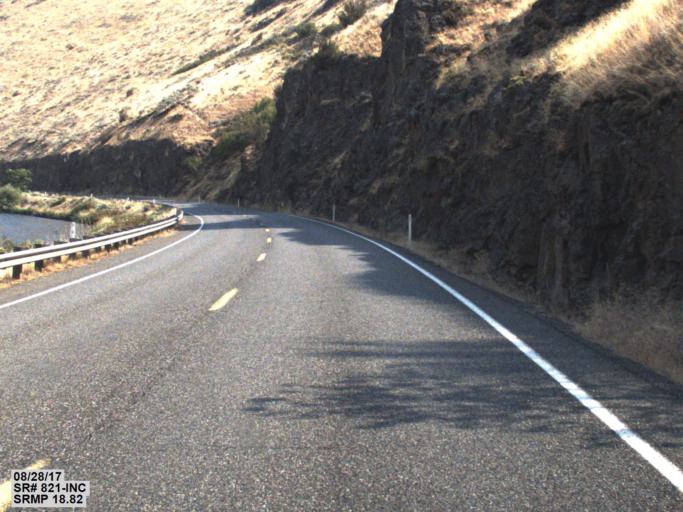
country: US
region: Washington
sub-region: Kittitas County
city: Kittitas
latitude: 46.8756
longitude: -120.4878
